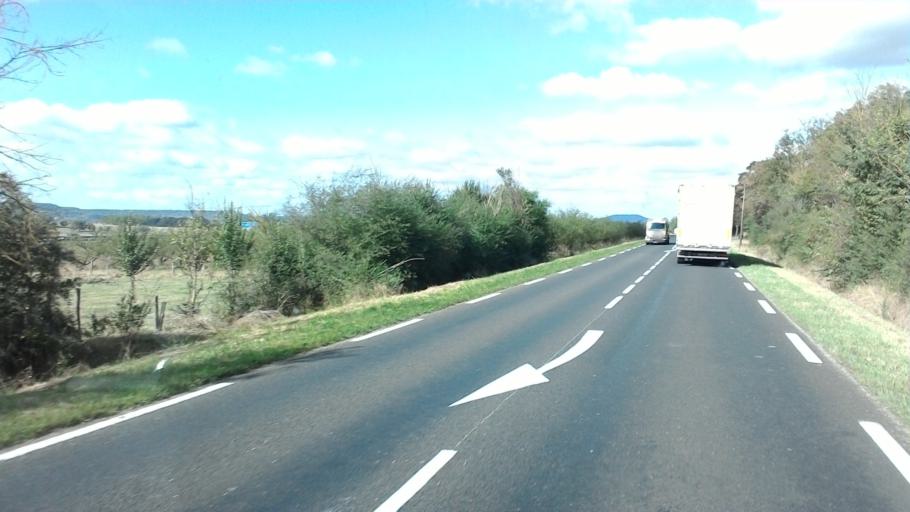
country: FR
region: Lorraine
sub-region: Departement de Meurthe-et-Moselle
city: Blenod-les-Toul
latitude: 48.5864
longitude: 5.8896
